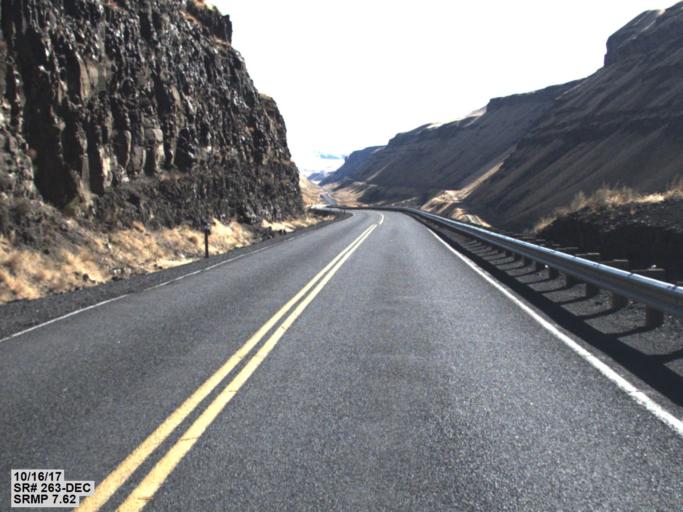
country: US
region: Washington
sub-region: Franklin County
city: Connell
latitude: 46.6239
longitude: -118.5597
